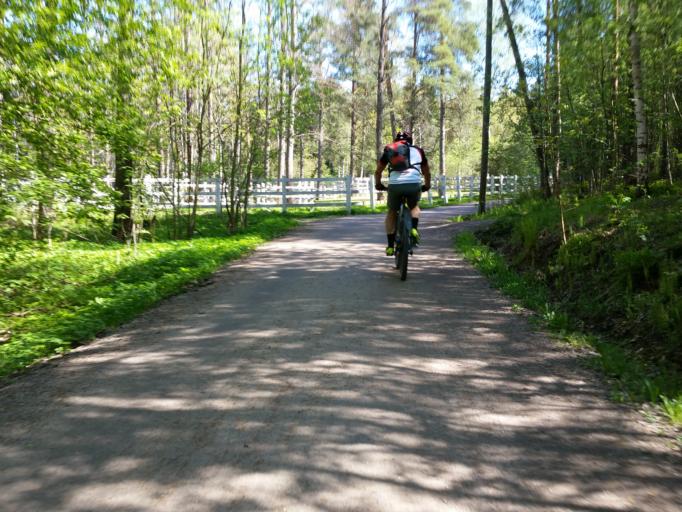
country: FI
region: Uusimaa
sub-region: Helsinki
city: Helsinki
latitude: 60.1971
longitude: 24.9122
